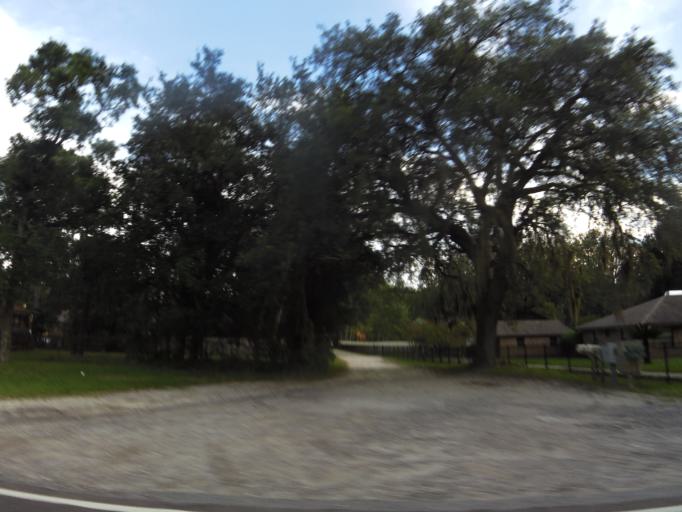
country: US
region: Florida
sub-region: Saint Johns County
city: Fruit Cove
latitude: 30.1390
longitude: -81.6008
